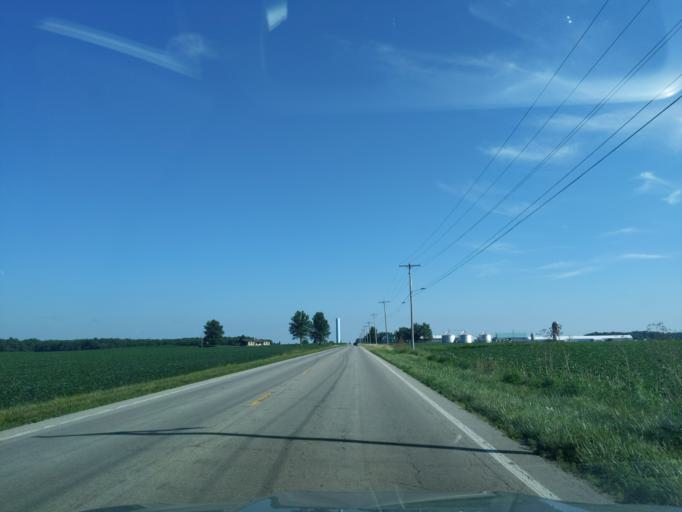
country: US
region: Indiana
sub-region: Ripley County
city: Osgood
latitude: 39.1899
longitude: -85.3228
